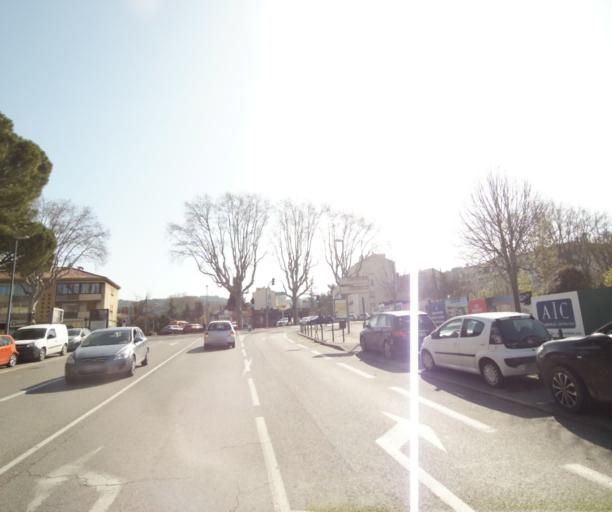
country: FR
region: Provence-Alpes-Cote d'Azur
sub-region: Departement des Bouches-du-Rhone
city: Aix-en-Provence
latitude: 43.5096
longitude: 5.4400
